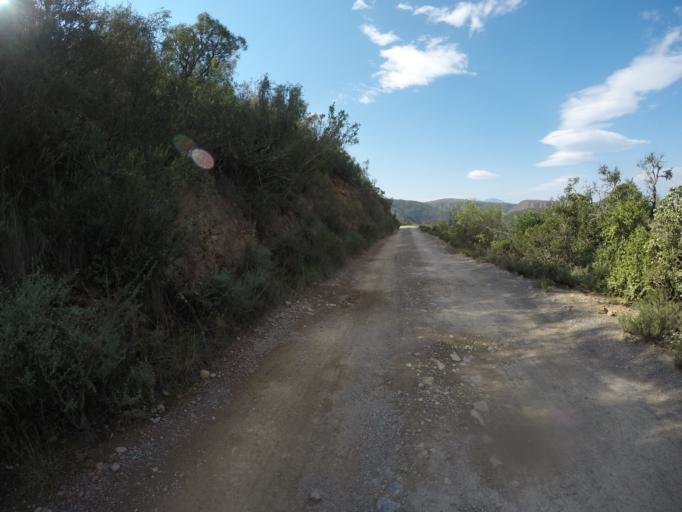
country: ZA
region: Eastern Cape
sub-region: Cacadu District Municipality
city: Kareedouw
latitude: -33.6490
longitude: 24.3475
